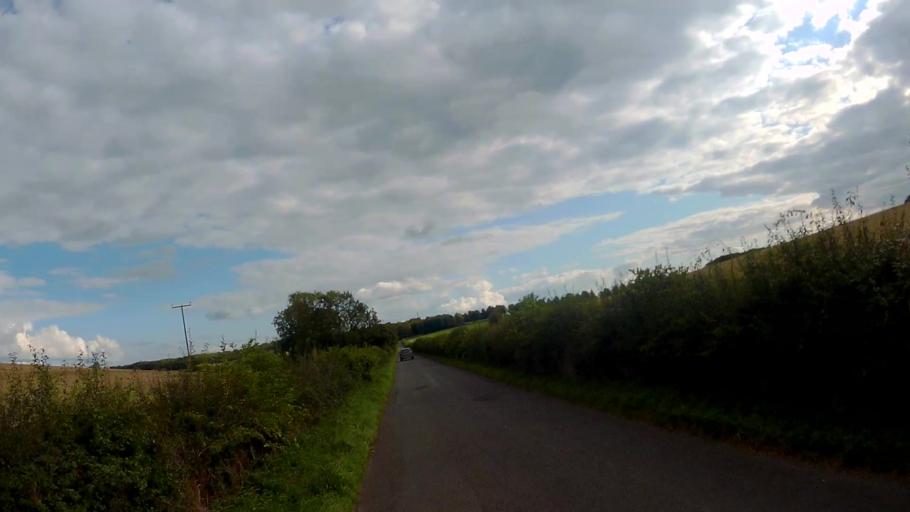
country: GB
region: England
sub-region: Hampshire
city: Kings Worthy
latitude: 51.1409
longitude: -1.2130
